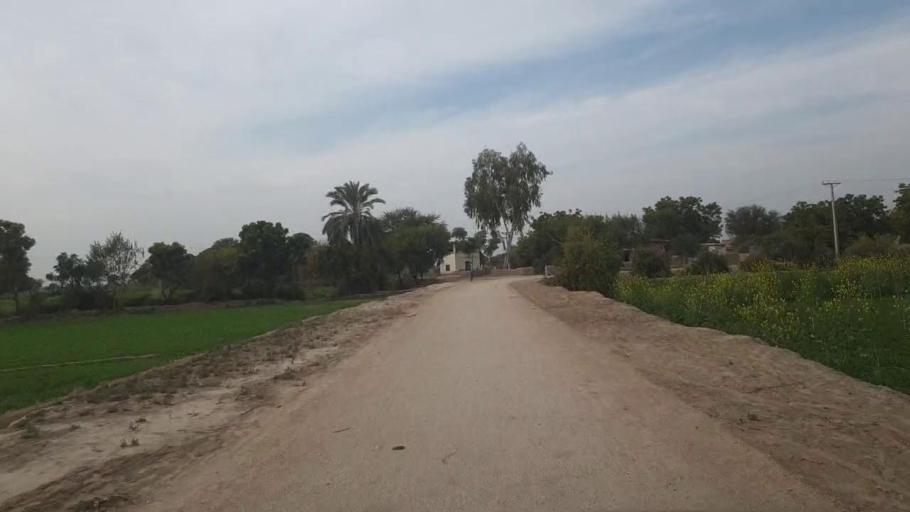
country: PK
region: Sindh
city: Shahpur Chakar
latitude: 26.1153
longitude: 68.5197
